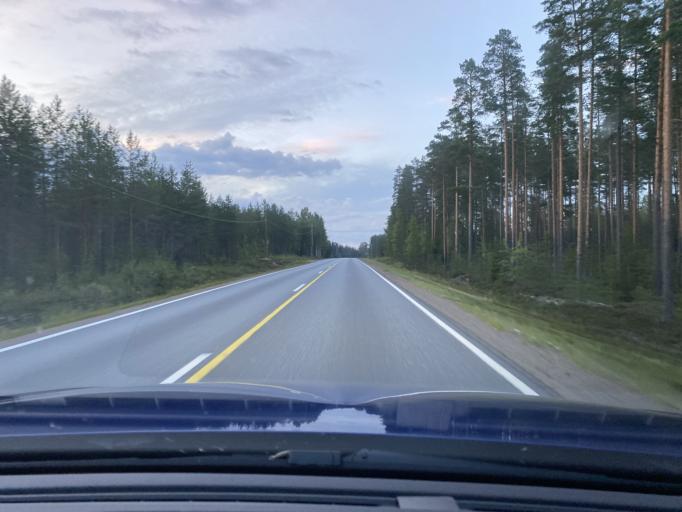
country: FI
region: Satakunta
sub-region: Pohjois-Satakunta
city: Honkajoki
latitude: 62.1643
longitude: 22.2694
